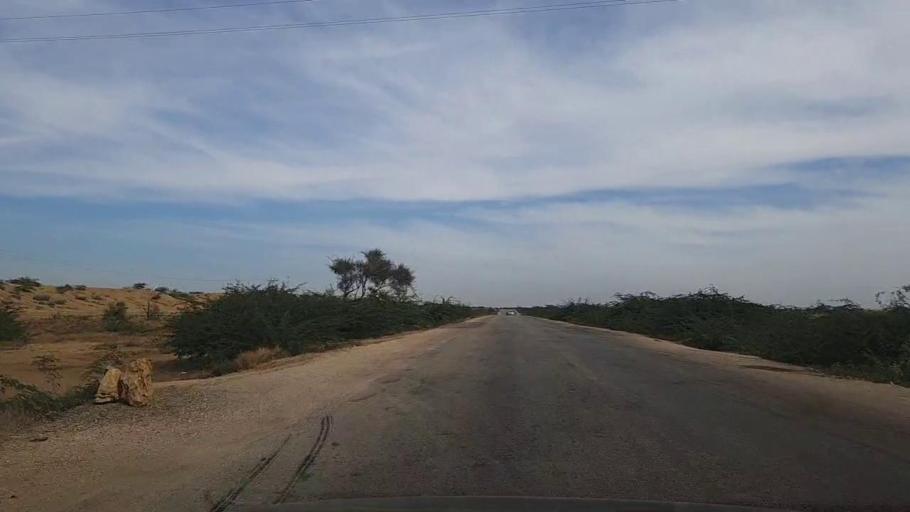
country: PK
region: Sindh
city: Thatta
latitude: 24.8643
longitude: 68.0276
